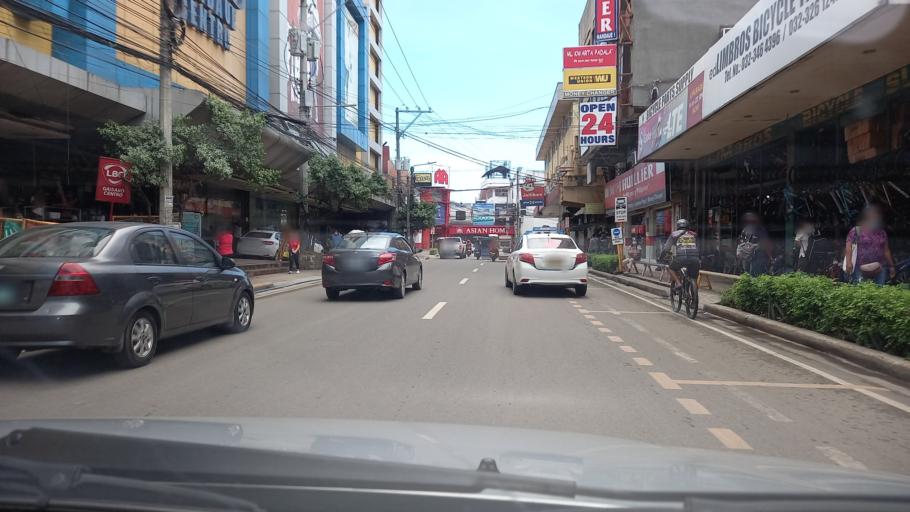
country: PH
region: Central Visayas
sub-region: Lapu-Lapu City
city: Buagsong
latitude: 10.3285
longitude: 123.9420
